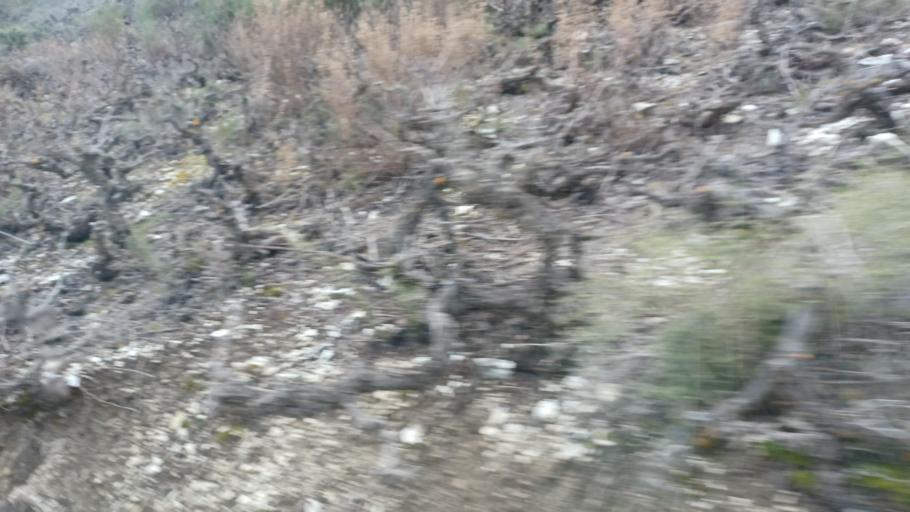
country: CY
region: Limassol
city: Pachna
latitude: 34.8688
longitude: 32.7974
